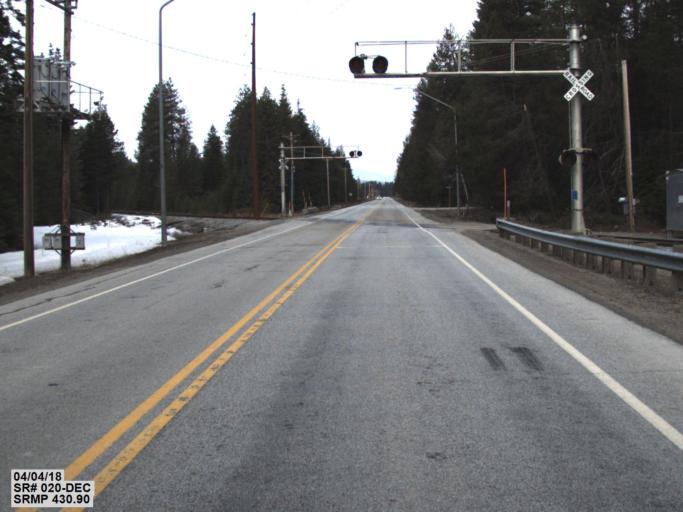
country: US
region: Washington
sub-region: Pend Oreille County
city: Newport
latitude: 48.2273
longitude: -117.1430
